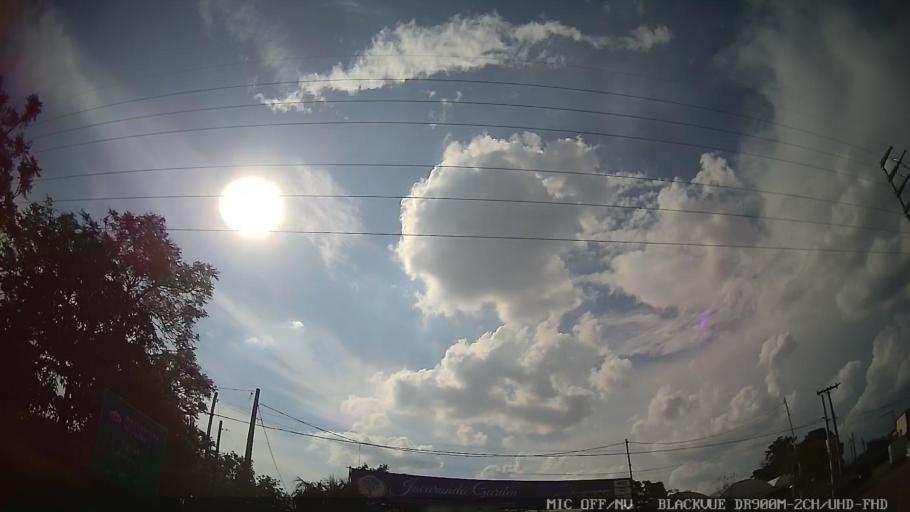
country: BR
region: Sao Paulo
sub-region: Braganca Paulista
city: Braganca Paulista
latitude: -22.9292
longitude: -46.5549
